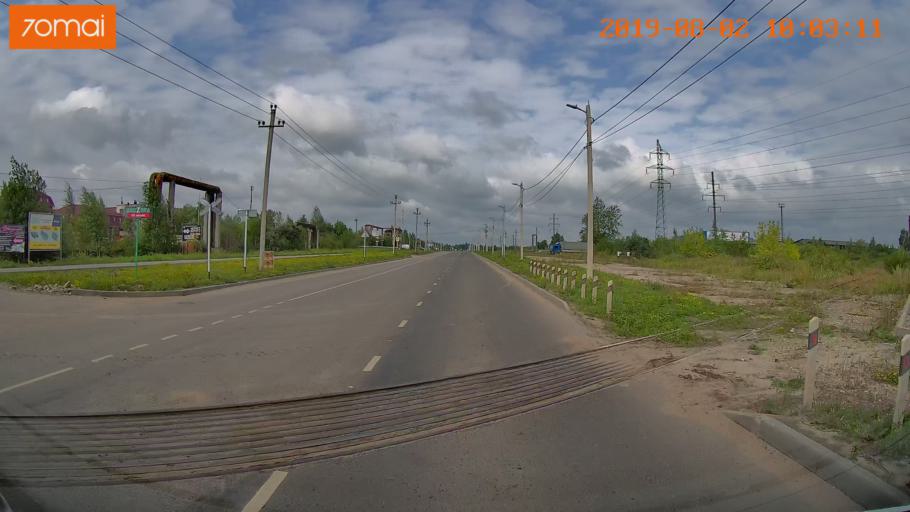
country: RU
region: Ivanovo
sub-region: Gorod Ivanovo
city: Ivanovo
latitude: 56.9661
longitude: 40.9464
